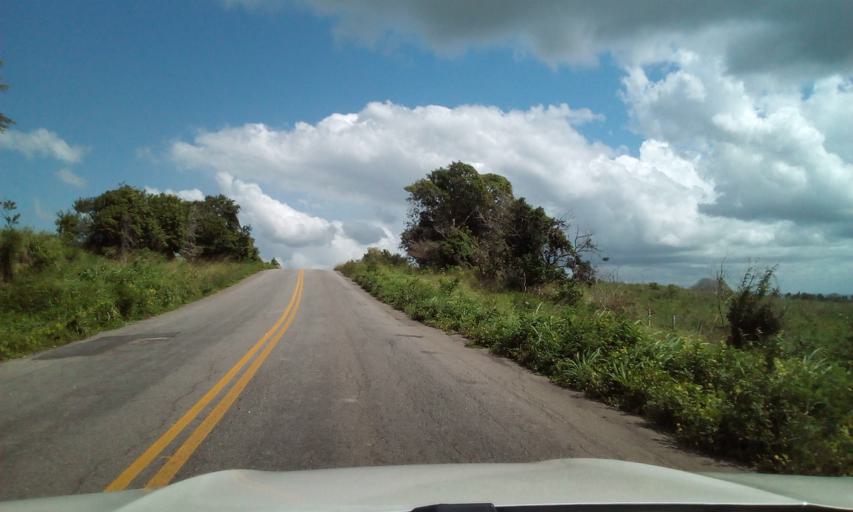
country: BR
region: Paraiba
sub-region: Guarabira
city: Guarabira
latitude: -6.8580
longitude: -35.4154
